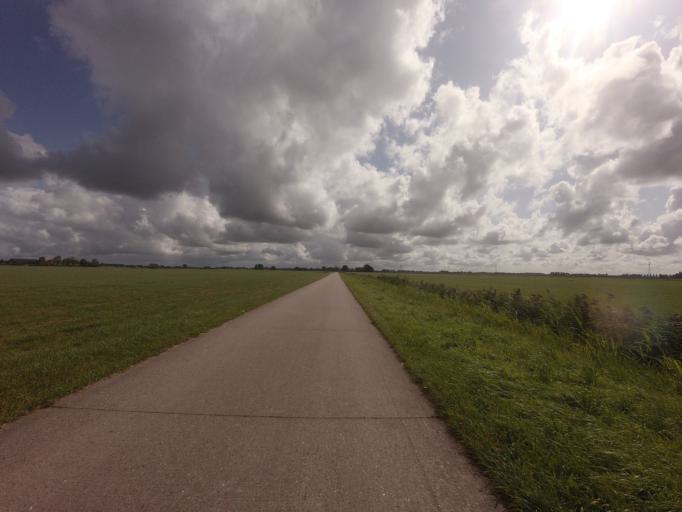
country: NL
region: Friesland
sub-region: Sudwest Fryslan
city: Scharnegoutum
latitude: 53.0704
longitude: 5.6374
